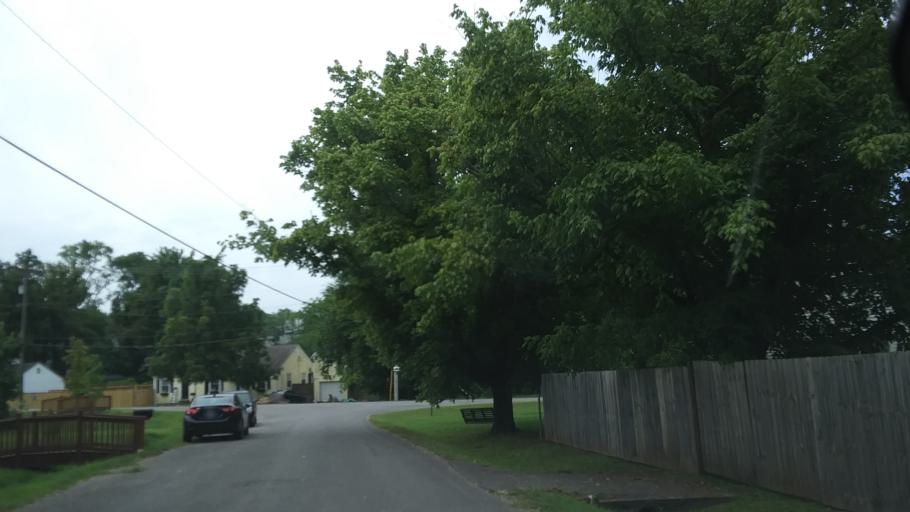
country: US
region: Tennessee
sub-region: Davidson County
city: Belle Meade
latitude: 36.1515
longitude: -86.8722
